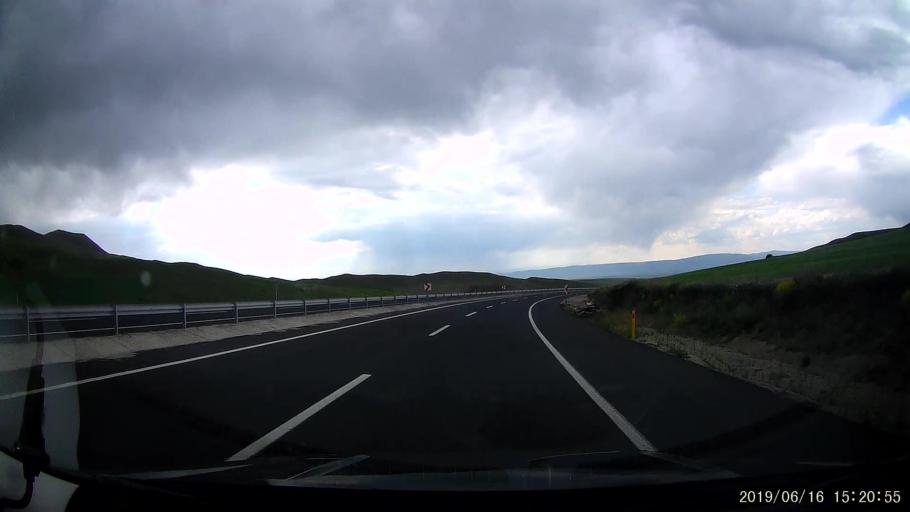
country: TR
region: Erzurum
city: Aras
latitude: 39.9729
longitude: 42.2539
